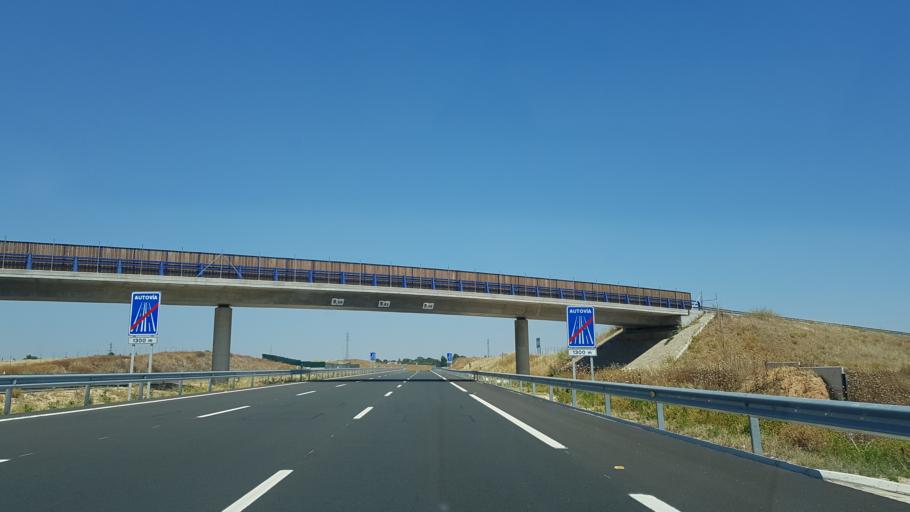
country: ES
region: Andalusia
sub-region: Provincia de Sevilla
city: Coria del Rio
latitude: 37.2986
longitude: -6.0688
